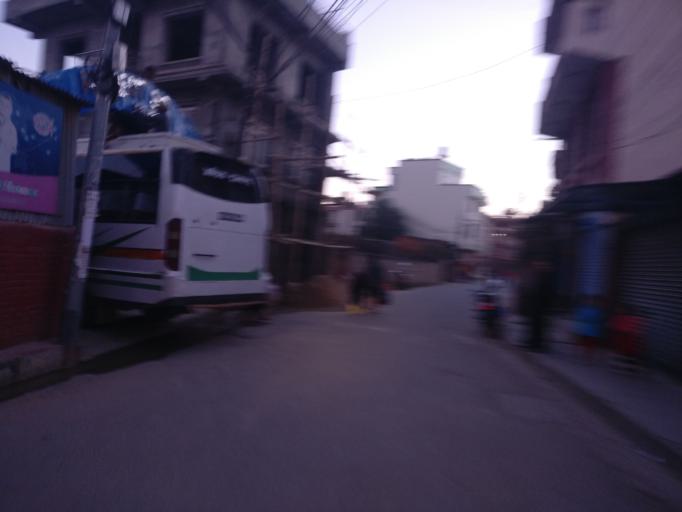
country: NP
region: Central Region
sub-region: Bagmati Zone
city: Patan
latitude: 27.6532
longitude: 85.3205
